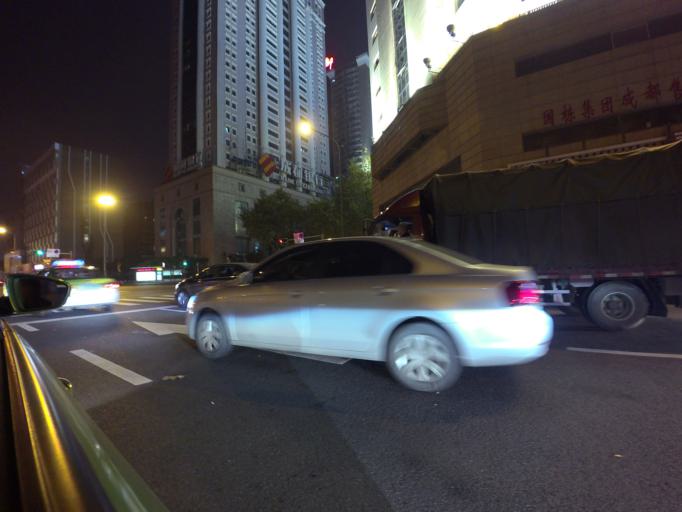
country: CN
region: Sichuan
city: Chengdu
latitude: 30.6585
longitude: 104.0583
